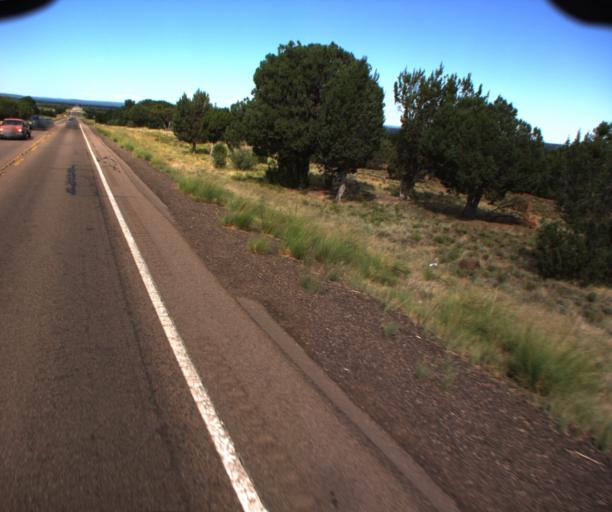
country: US
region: Arizona
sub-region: Navajo County
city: White Mountain Lake
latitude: 34.2734
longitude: -109.9091
